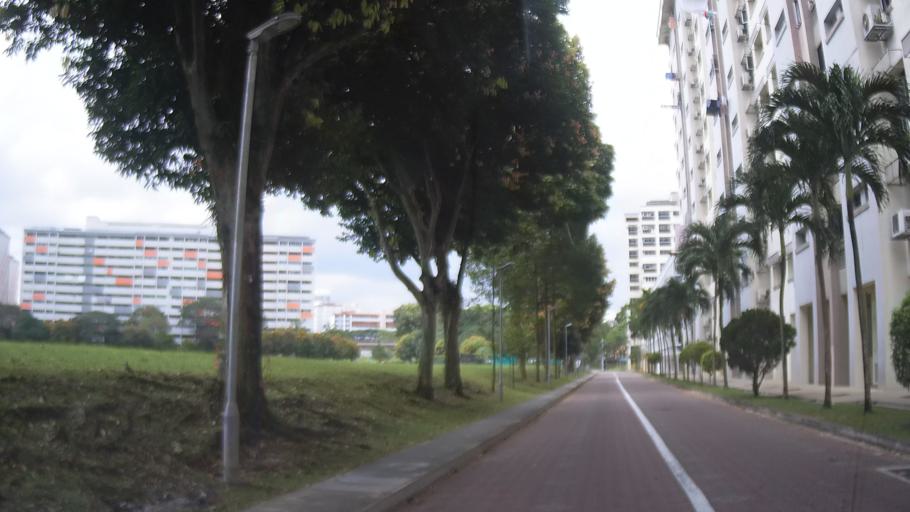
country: MY
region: Johor
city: Johor Bahru
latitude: 1.4321
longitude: 103.7841
